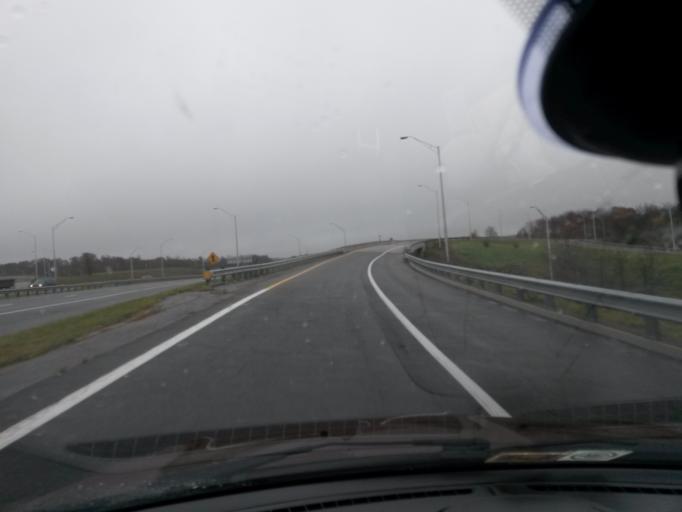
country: US
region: Virginia
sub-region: Montgomery County
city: Christiansburg
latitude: 37.1327
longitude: -80.3732
